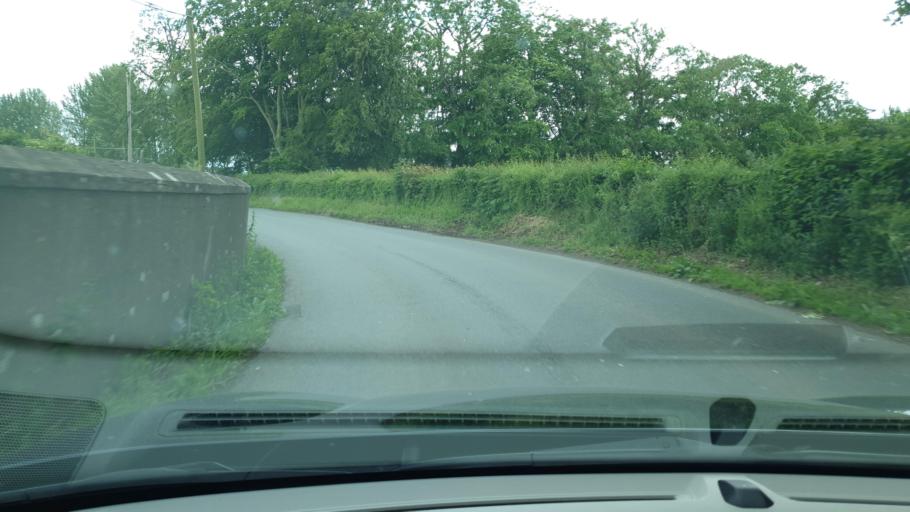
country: IE
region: Leinster
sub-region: An Mhi
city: Dunboyne
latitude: 53.4032
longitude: -6.4725
